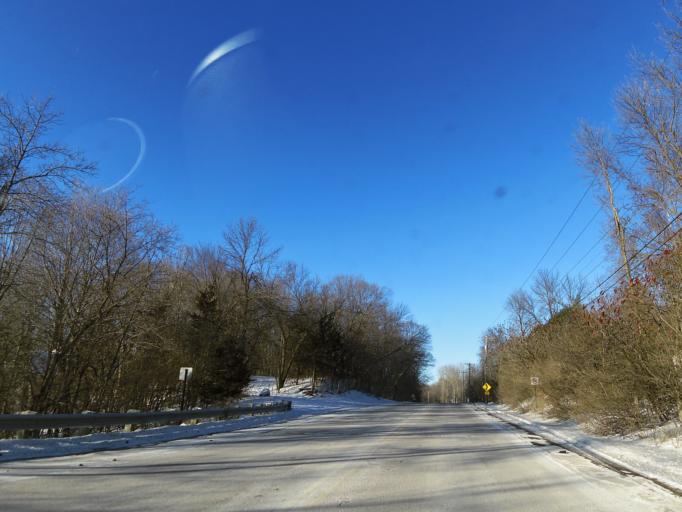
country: US
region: Minnesota
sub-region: Hennepin County
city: Mound
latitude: 44.8982
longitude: -93.6770
